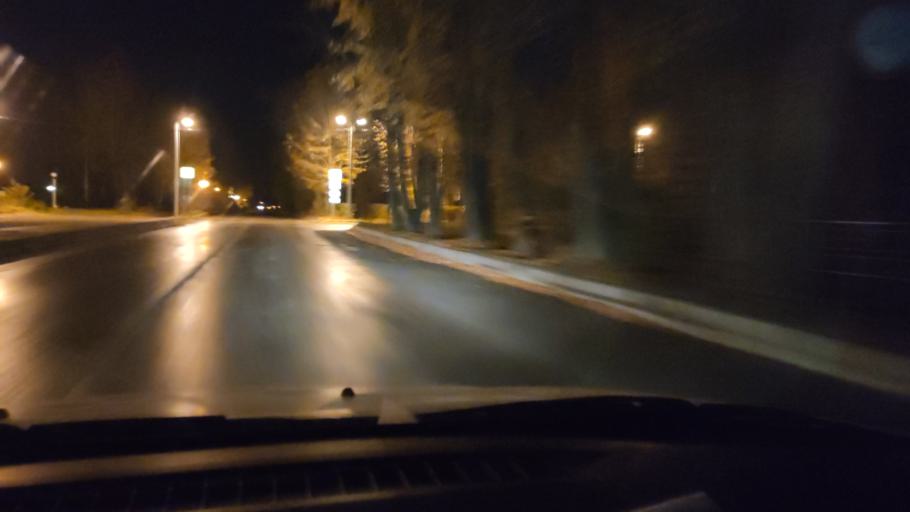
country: RU
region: Perm
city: Overyata
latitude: 58.0169
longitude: 55.9093
